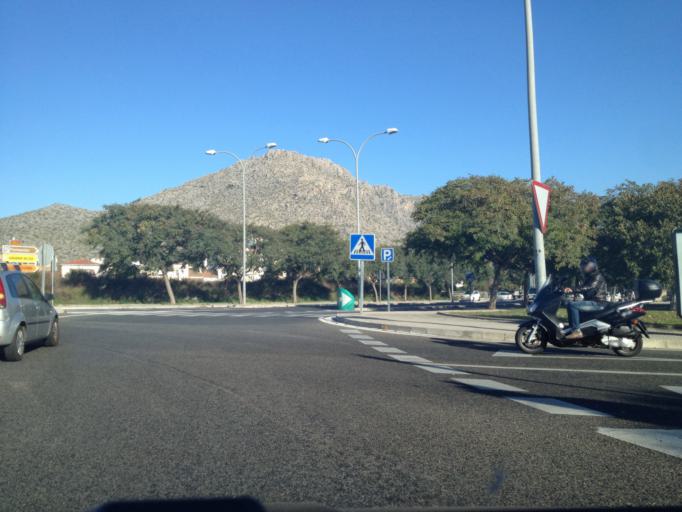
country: ES
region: Balearic Islands
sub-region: Illes Balears
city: Pollenca
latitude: 39.9045
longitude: 3.0755
